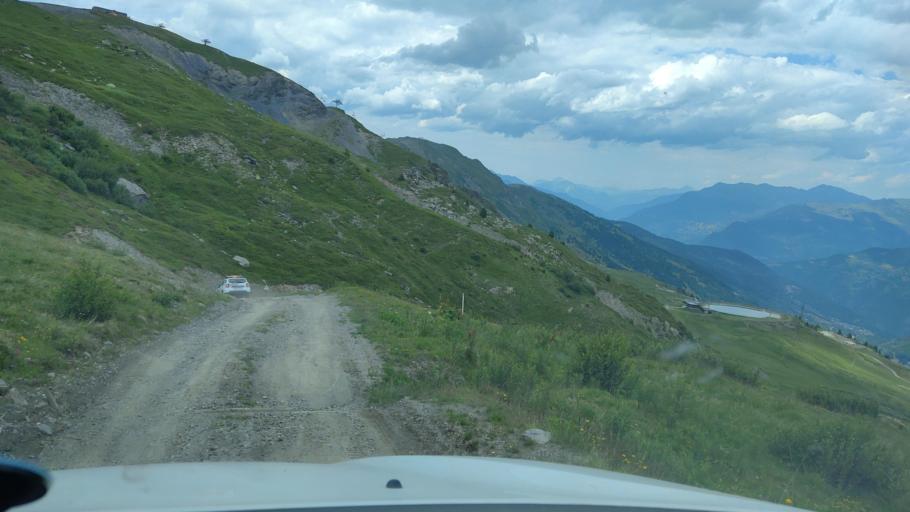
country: FR
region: Rhone-Alpes
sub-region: Departement de la Savoie
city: Meribel
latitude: 45.3715
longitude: 6.5568
